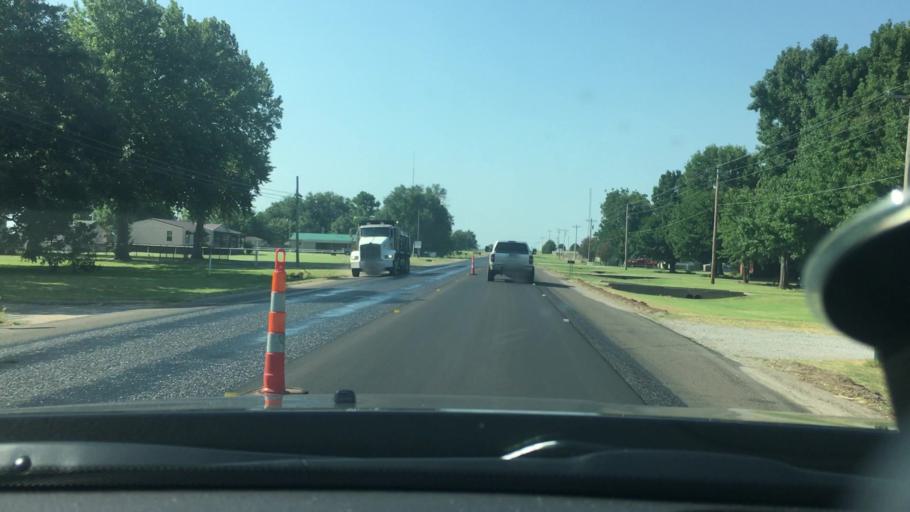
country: US
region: Oklahoma
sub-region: Garvin County
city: Lindsay
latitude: 34.8078
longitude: -97.5983
